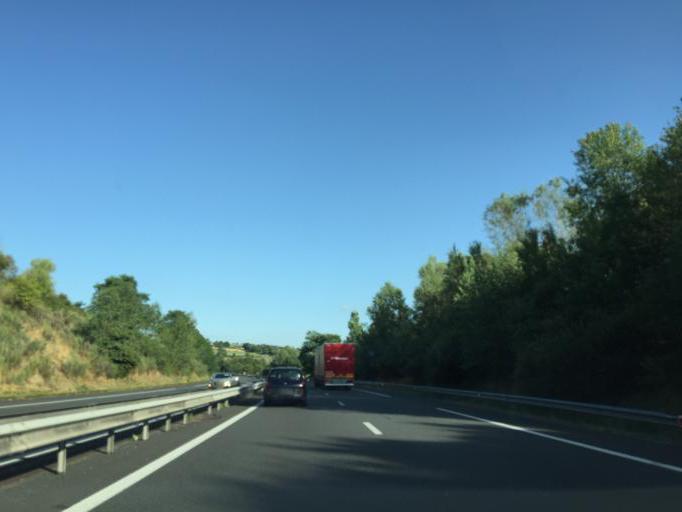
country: FR
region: Auvergne
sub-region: Departement de l'Allier
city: Montmarault
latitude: 46.3339
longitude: 2.8901
